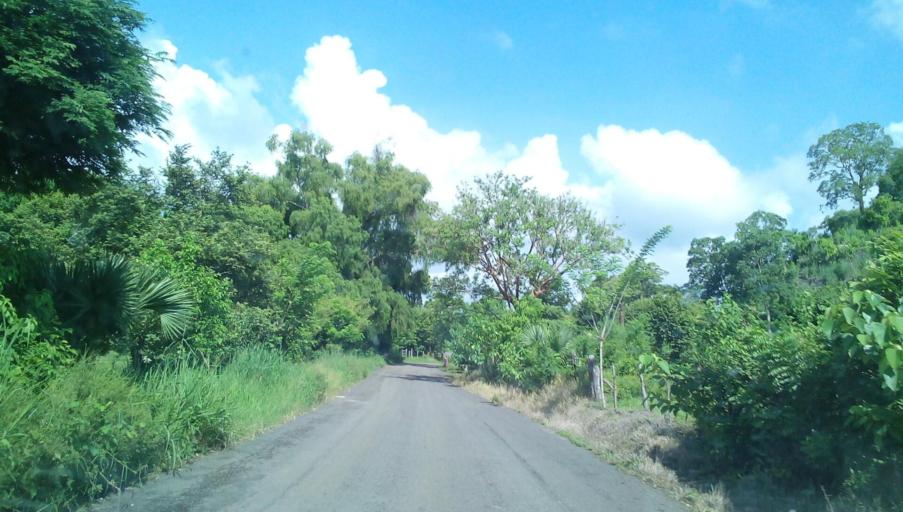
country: MX
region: Veracruz
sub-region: Citlaltepetl
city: Las Sabinas
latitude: 21.3424
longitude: -97.8870
